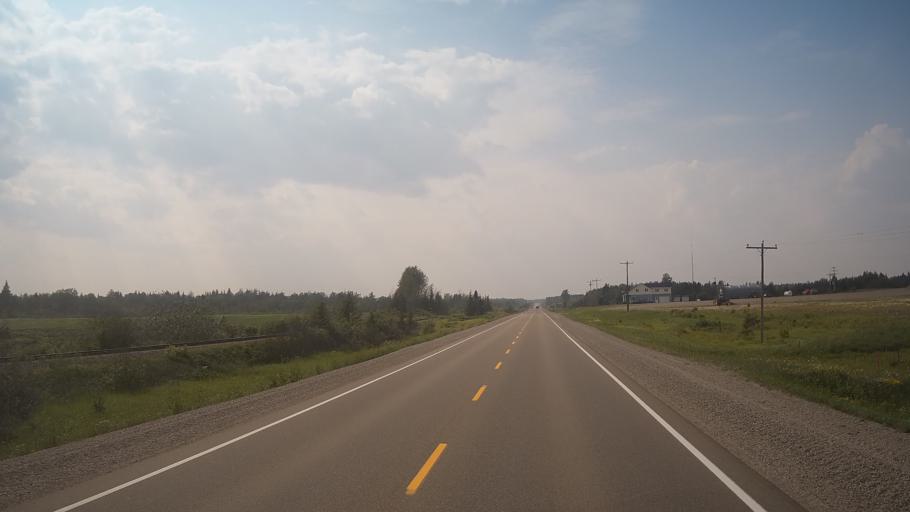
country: CA
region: Ontario
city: Kapuskasing
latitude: 49.4875
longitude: -82.7142
